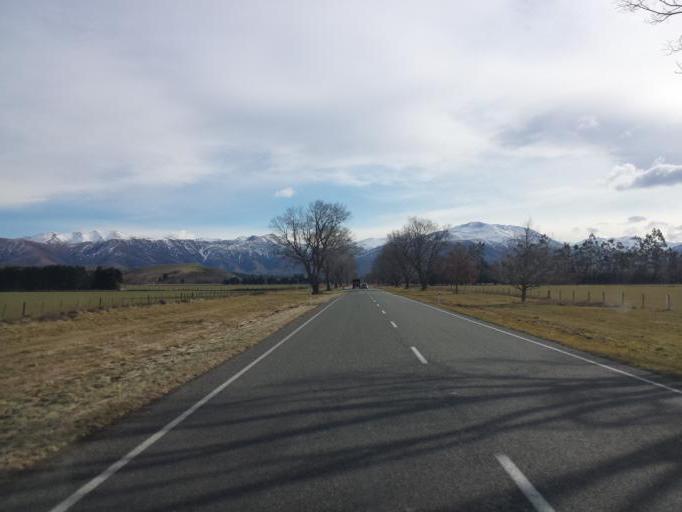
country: NZ
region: Canterbury
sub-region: Timaru District
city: Pleasant Point
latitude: -44.0679
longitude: 170.7876
